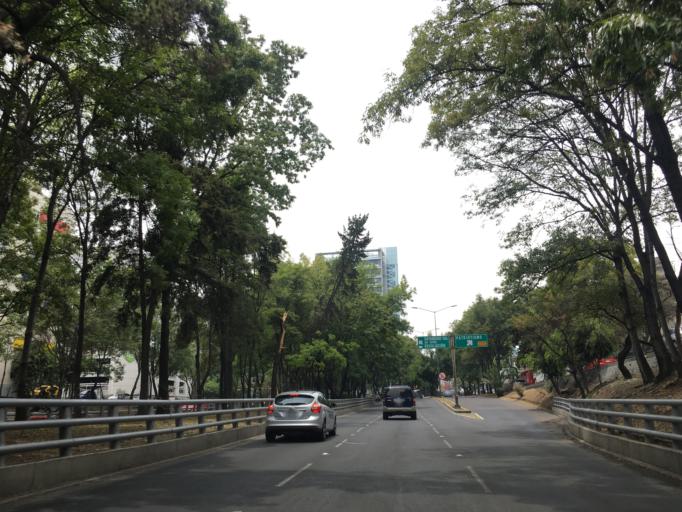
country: MX
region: Mexico City
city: Colonia del Valle
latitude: 19.3977
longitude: -99.1777
